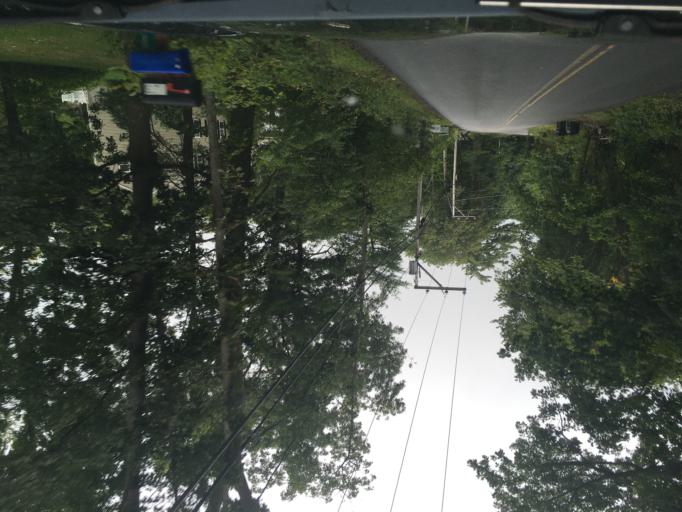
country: US
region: New Hampshire
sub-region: Rockingham County
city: Exeter
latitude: 42.9902
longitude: -70.8956
